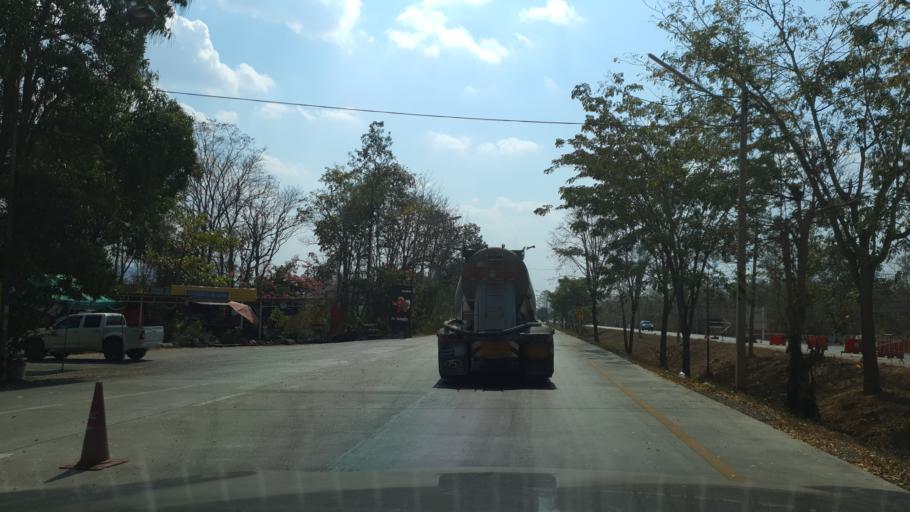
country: TH
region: Lampang
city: Mae Phrik
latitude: 17.4437
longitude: 99.1593
